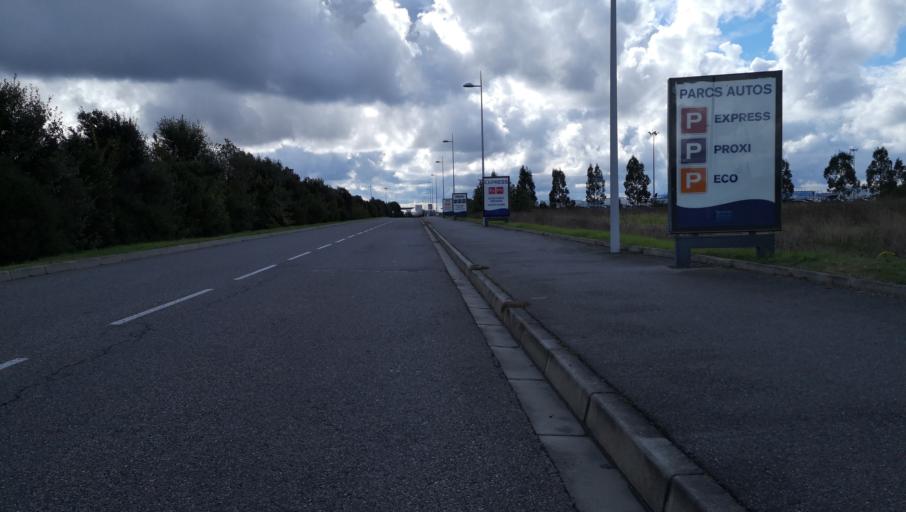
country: FR
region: Midi-Pyrenees
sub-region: Departement de la Haute-Garonne
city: Beauzelle
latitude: 43.6415
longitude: 1.3646
